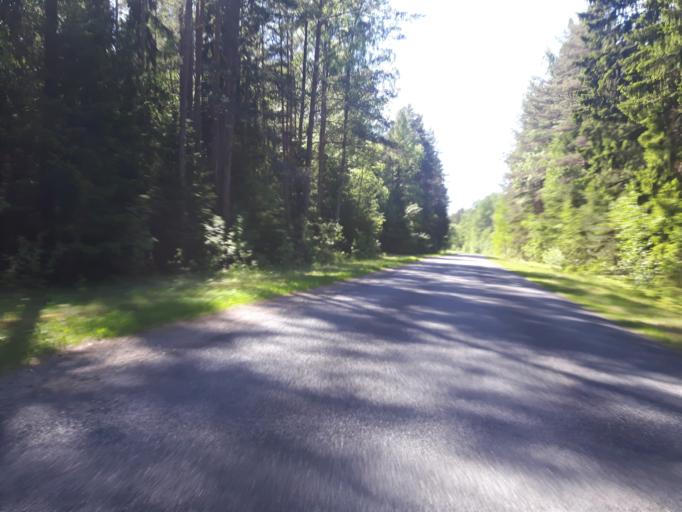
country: EE
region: Laeaene-Virumaa
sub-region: Haljala vald
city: Haljala
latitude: 59.5688
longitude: 26.2536
